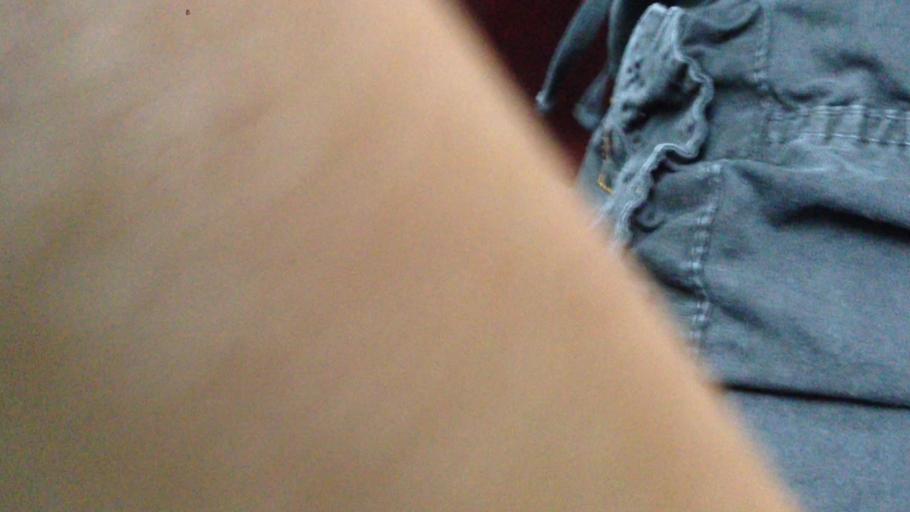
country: US
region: New York
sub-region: Dutchess County
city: Red Hook
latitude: 41.9817
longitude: -73.9171
